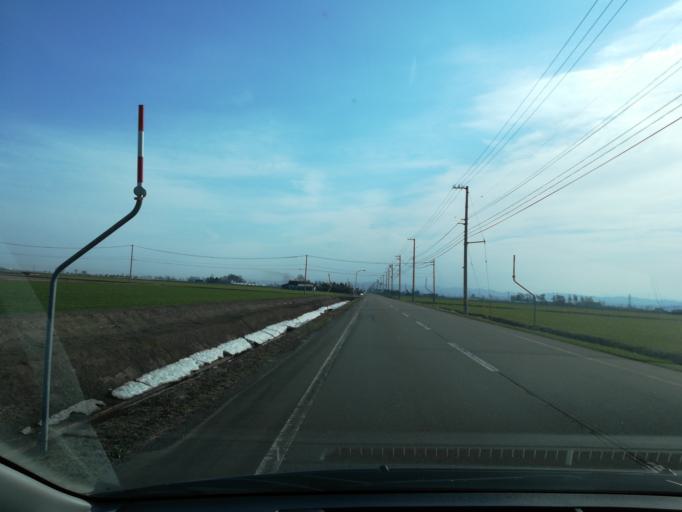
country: JP
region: Hokkaido
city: Iwamizawa
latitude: 43.1681
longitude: 141.6635
